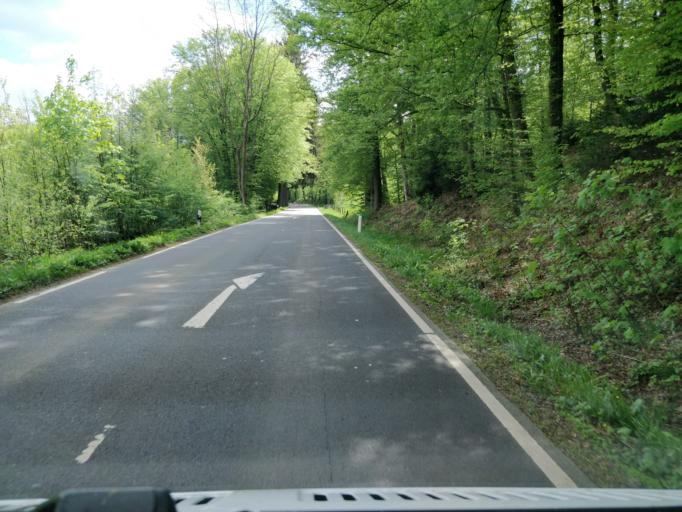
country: DE
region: North Rhine-Westphalia
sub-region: Regierungsbezirk Koln
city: Numbrecht
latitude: 50.9194
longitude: 7.5541
